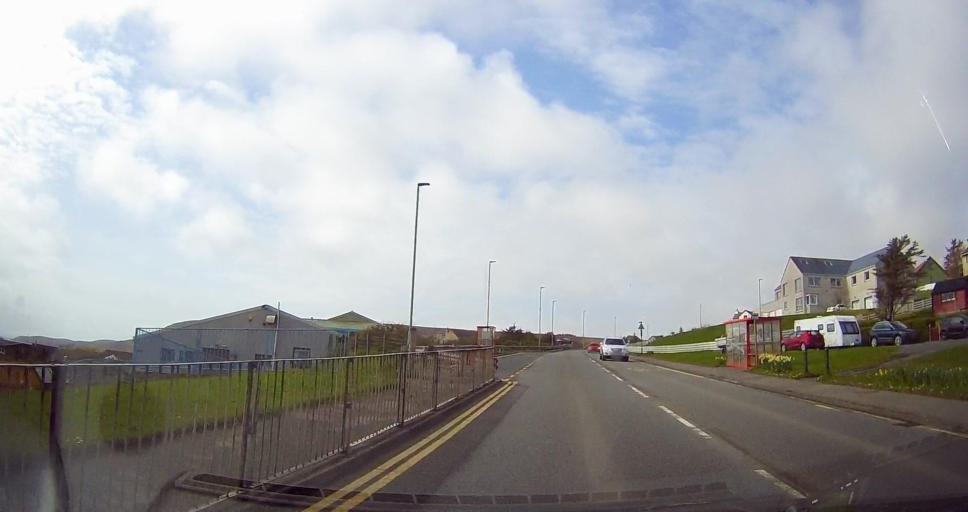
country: GB
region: Scotland
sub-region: Shetland Islands
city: Lerwick
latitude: 60.1451
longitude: -1.1718
